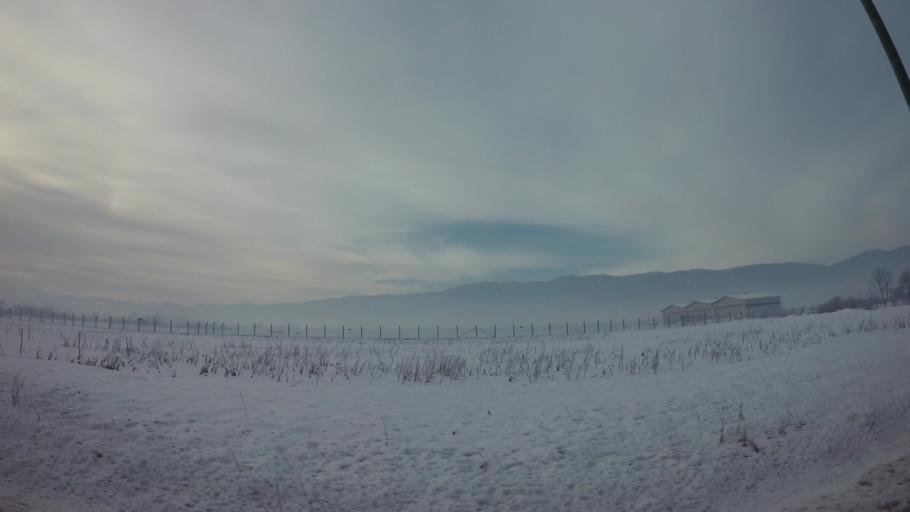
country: BA
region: Federation of Bosnia and Herzegovina
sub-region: Kanton Sarajevo
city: Sarajevo
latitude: 43.8237
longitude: 18.3478
